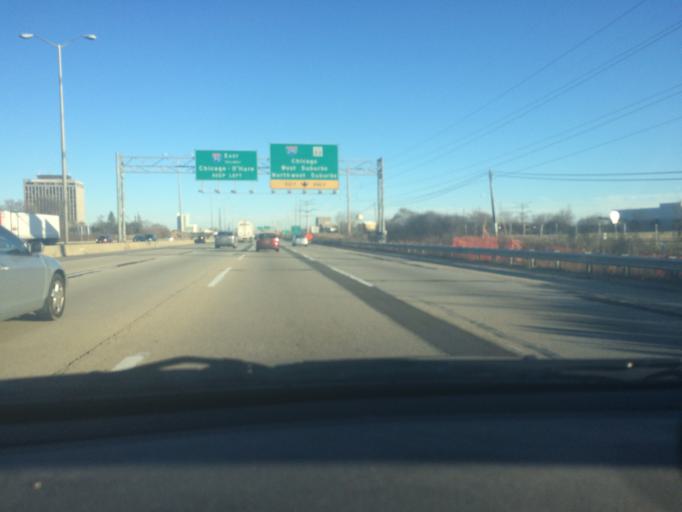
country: US
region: Illinois
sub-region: Cook County
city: Hoffman Estates
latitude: 42.0614
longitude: -88.0605
